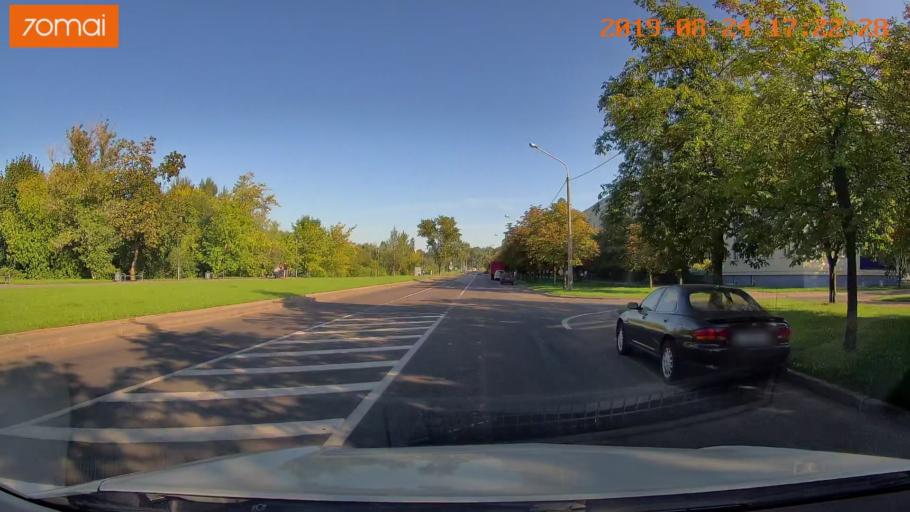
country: BY
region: Minsk
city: Hatava
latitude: 53.8456
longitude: 27.6447
